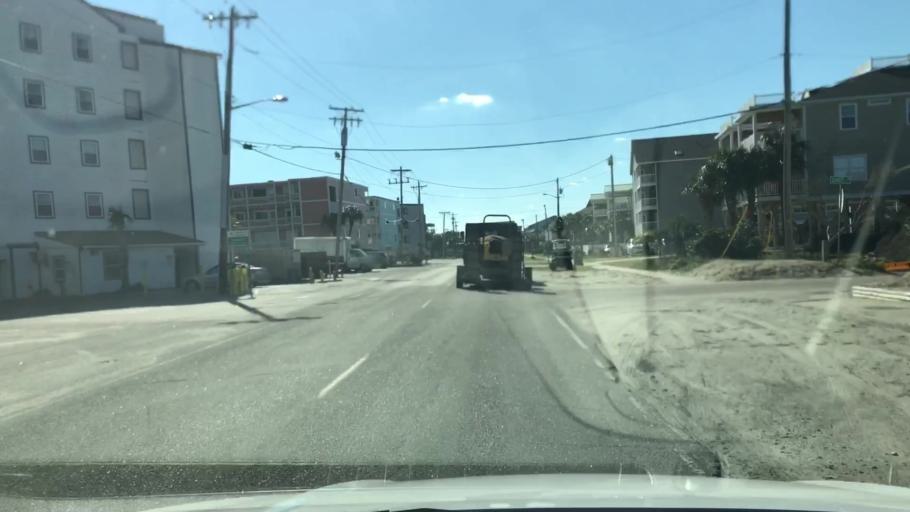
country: US
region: South Carolina
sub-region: Horry County
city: Garden City
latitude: 33.5842
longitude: -78.9923
